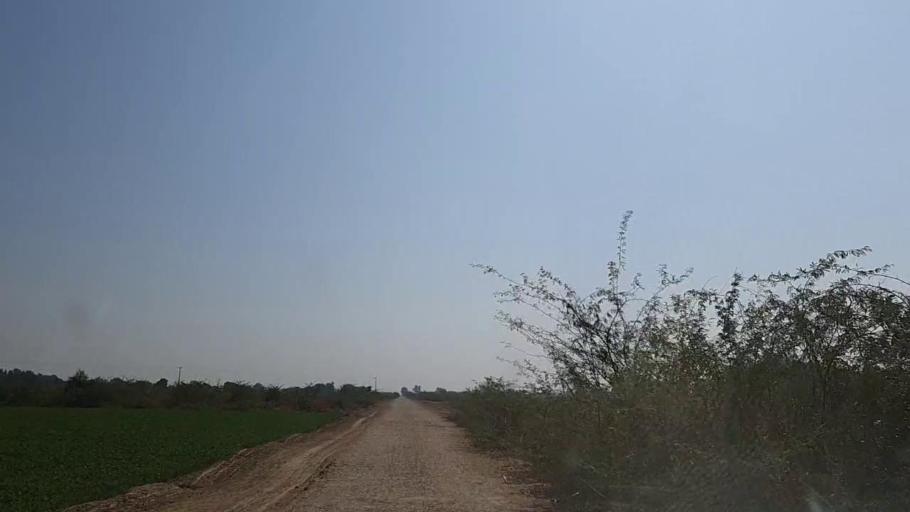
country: PK
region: Sindh
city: Digri
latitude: 24.9788
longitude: 69.2055
